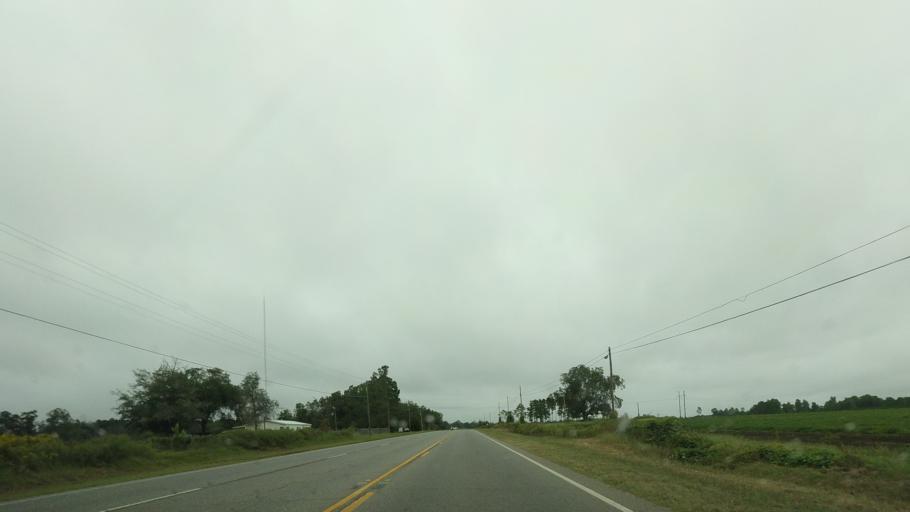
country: US
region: Georgia
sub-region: Ben Hill County
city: Fitzgerald
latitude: 31.6583
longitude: -83.2402
